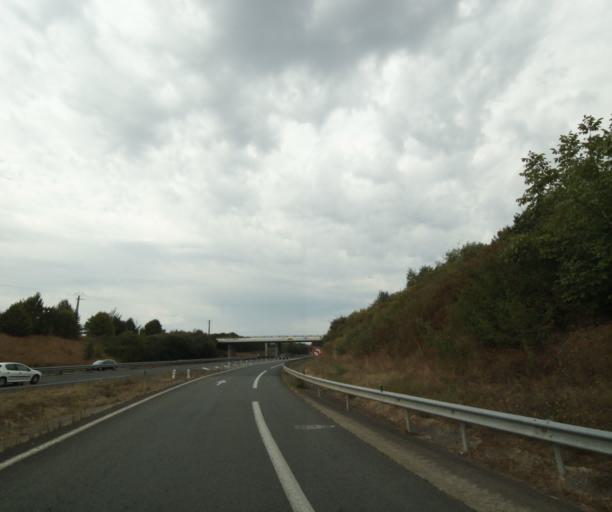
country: FR
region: Poitou-Charentes
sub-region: Departement de la Charente-Maritime
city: Tonnay-Charente
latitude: 45.9563
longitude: -0.8874
